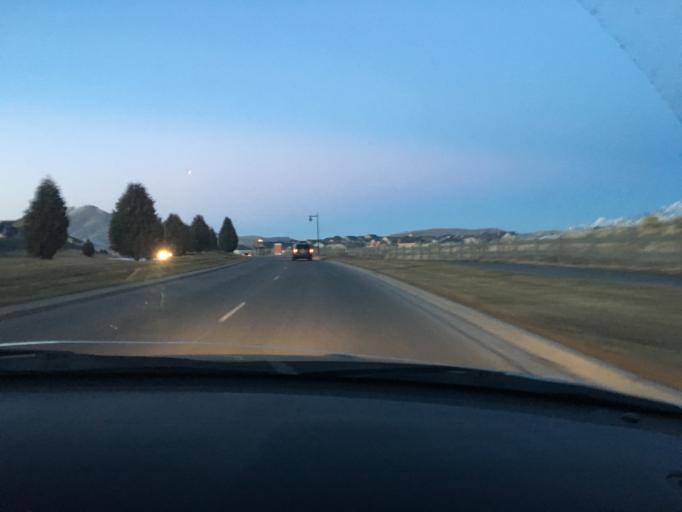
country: US
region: Utah
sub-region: Utah County
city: Eagle Mountain
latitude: 40.3722
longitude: -111.9743
